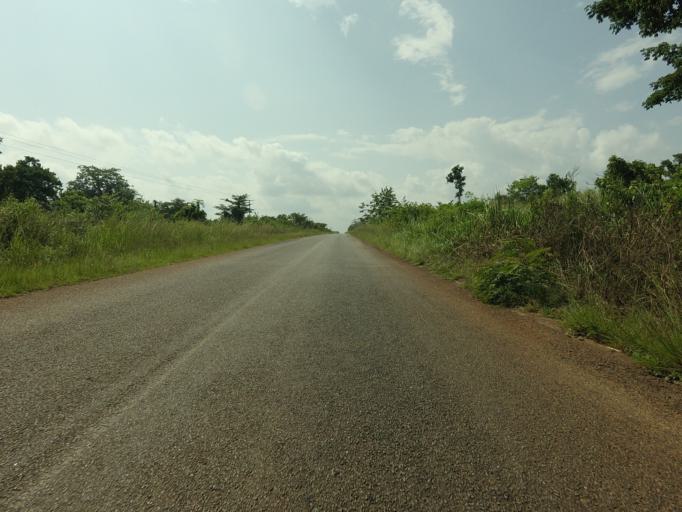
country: TG
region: Maritime
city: Tsevie
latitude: 6.3432
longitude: 0.8730
